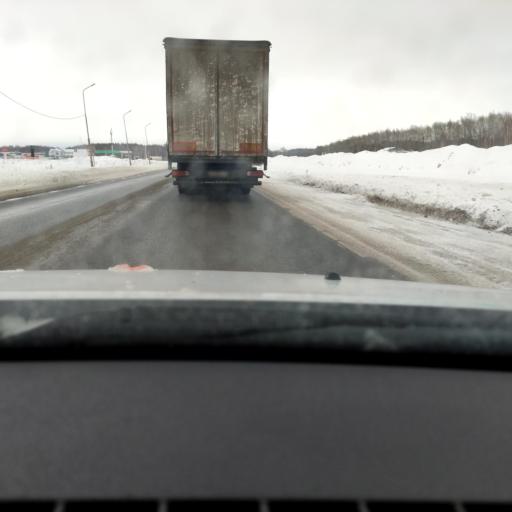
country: RU
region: Bashkortostan
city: Iglino
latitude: 54.7371
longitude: 56.2853
